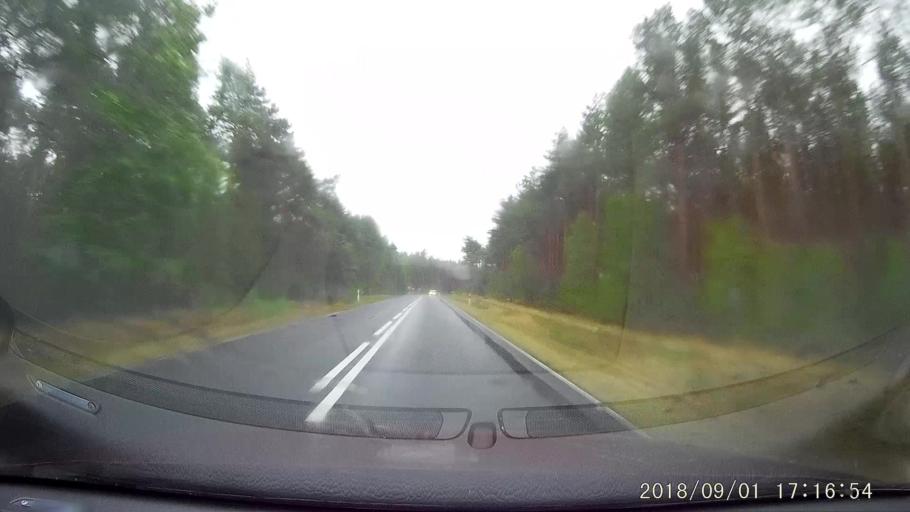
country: PL
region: Lubusz
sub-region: Powiat zielonogorski
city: Nowogrod Bobrzanski
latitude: 51.7574
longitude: 15.2709
